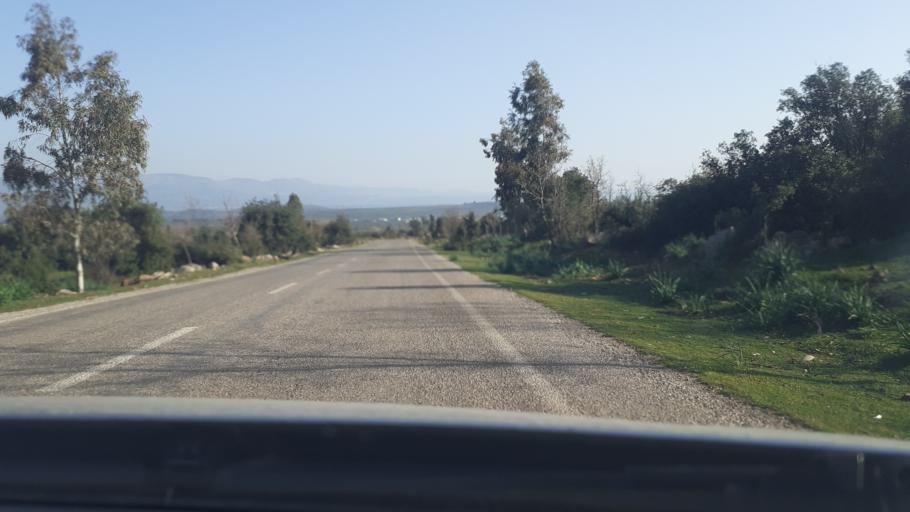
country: TR
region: Hatay
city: Aktepe
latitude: 36.7272
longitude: 36.4836
